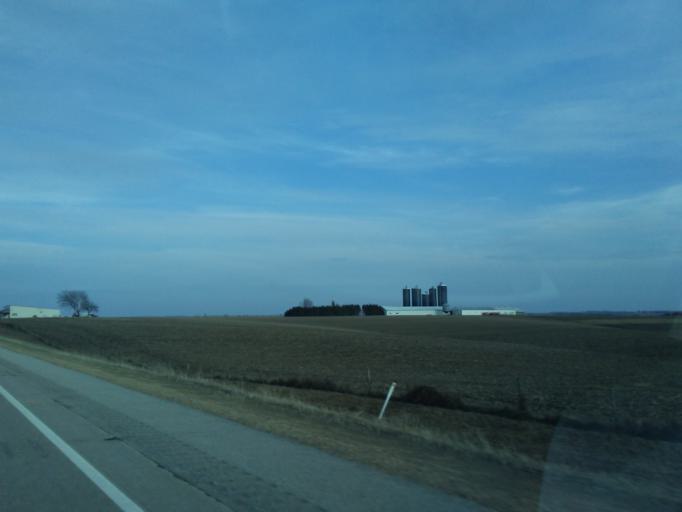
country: US
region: Wisconsin
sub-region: Iowa County
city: Dodgeville
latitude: 42.9757
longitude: -90.0271
